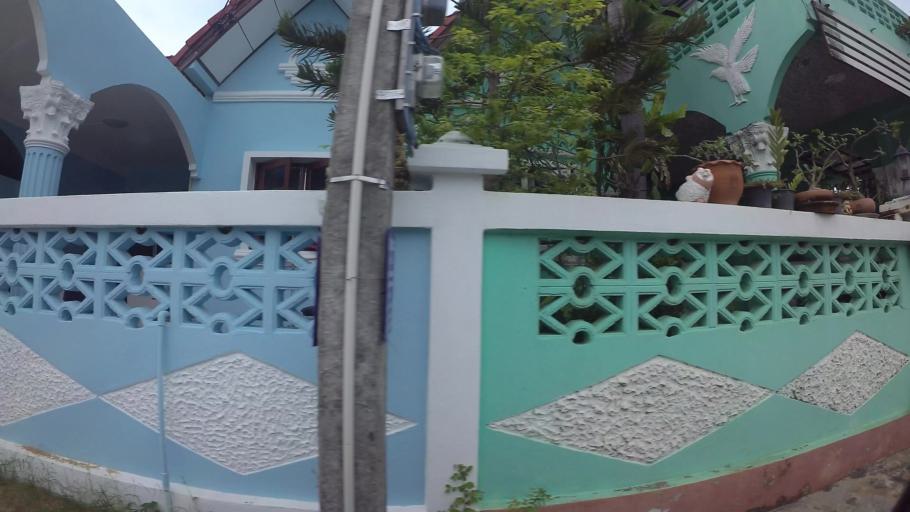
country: TH
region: Chon Buri
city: Sattahip
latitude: 12.6888
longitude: 100.8982
